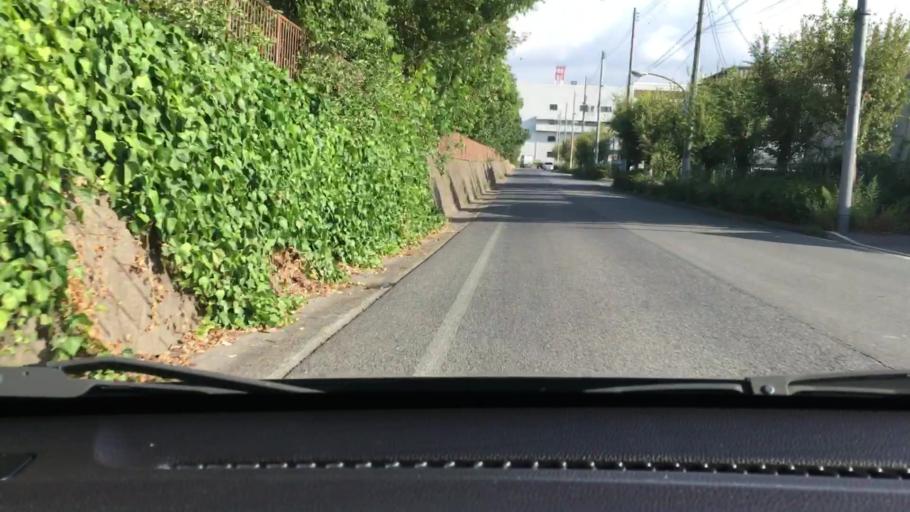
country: JP
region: Hyogo
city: Ashiya
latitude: 34.6922
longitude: 135.2752
